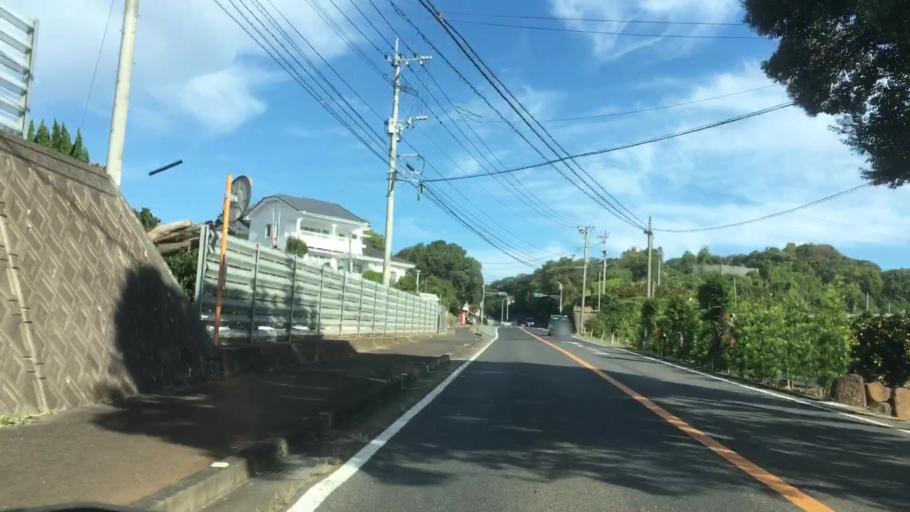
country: JP
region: Nagasaki
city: Sasebo
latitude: 33.0828
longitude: 129.7558
